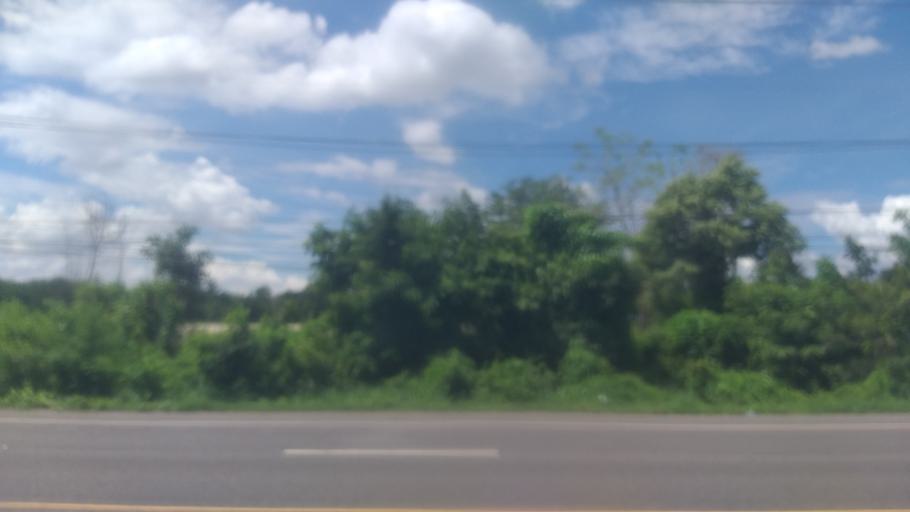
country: TH
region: Nakhon Ratchasima
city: Phra Thong Kham
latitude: 15.3003
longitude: 101.9800
